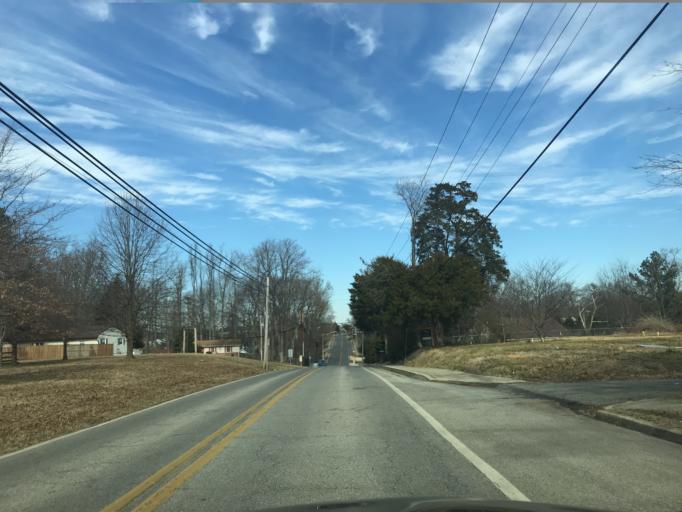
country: US
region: Maryland
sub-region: Charles County
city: La Plata
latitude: 38.5195
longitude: -76.9779
